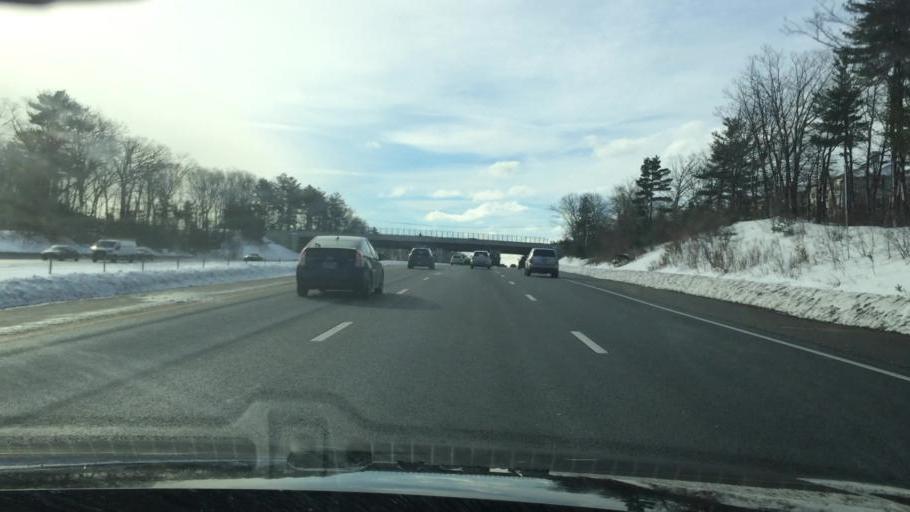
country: US
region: Massachusetts
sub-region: Middlesex County
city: Billerica
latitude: 42.5448
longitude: -71.2853
